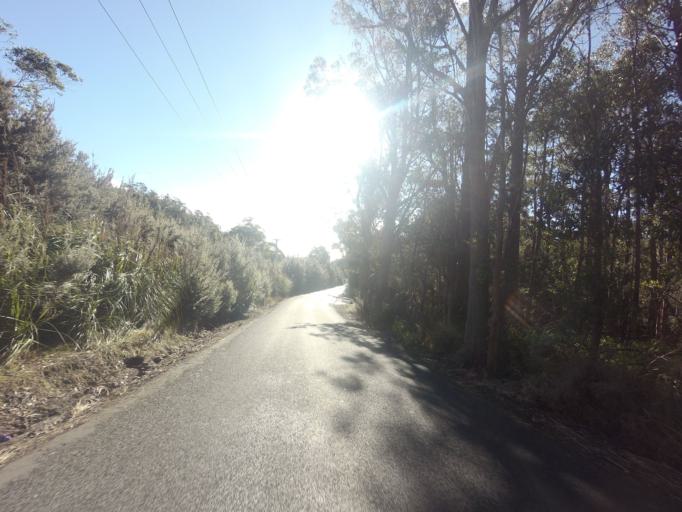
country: AU
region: Tasmania
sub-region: Glenorchy
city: Berriedale
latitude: -42.8413
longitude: 147.1581
